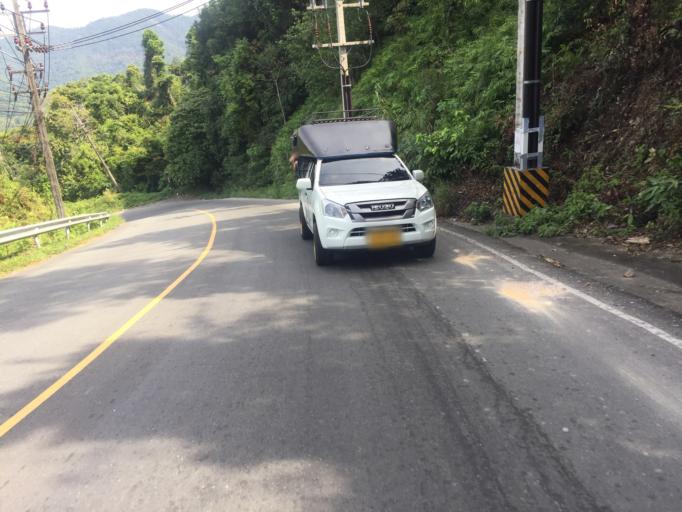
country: TH
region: Trat
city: Laem Ngop
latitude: 12.1251
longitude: 102.2696
